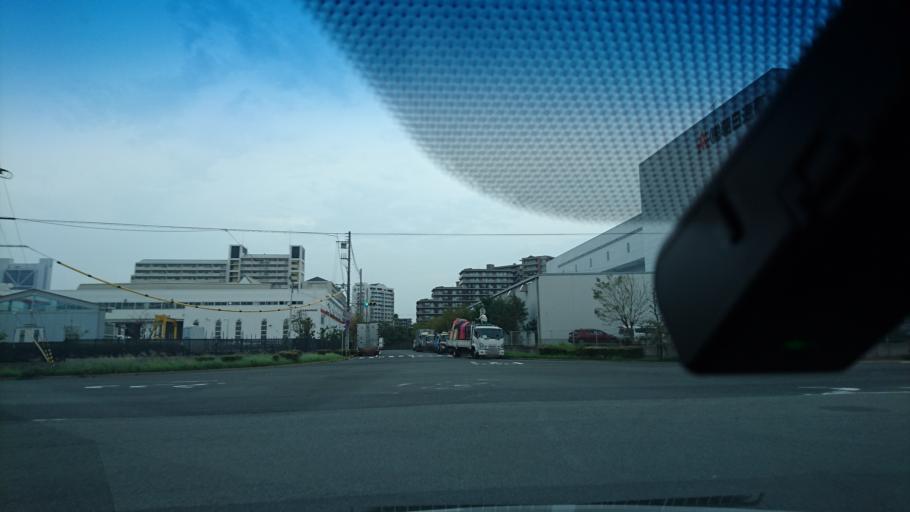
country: JP
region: Hyogo
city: Ashiya
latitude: 34.6851
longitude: 135.2613
